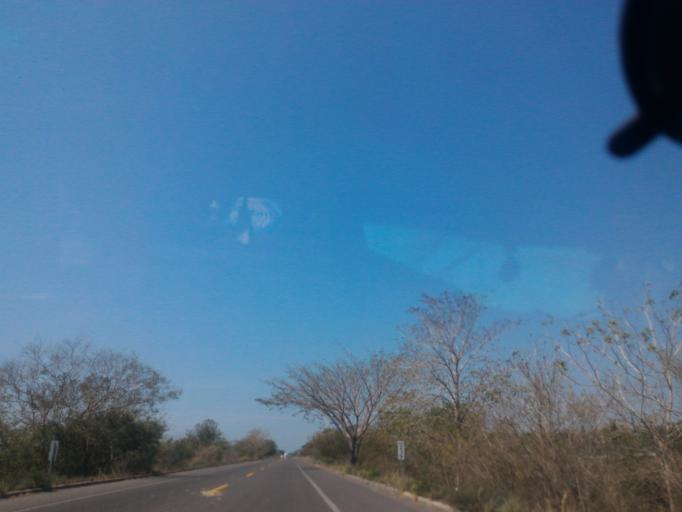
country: MX
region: Michoacan
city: Coahuayana Viejo
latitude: 18.7803
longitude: -103.7636
